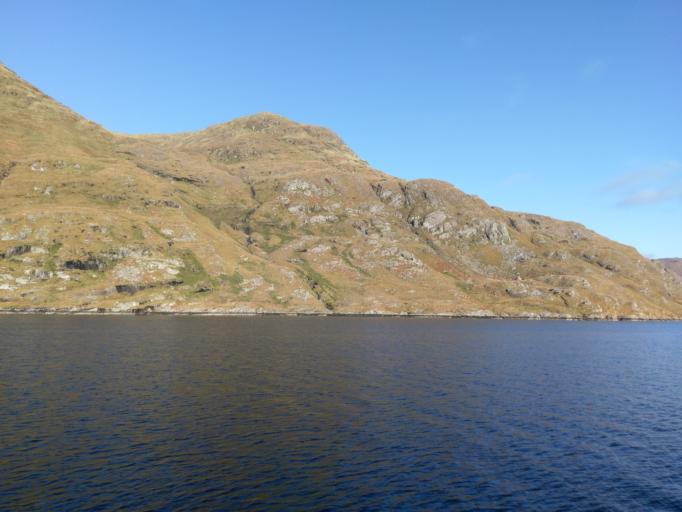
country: IE
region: Connaught
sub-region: County Galway
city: Clifden
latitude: 53.6191
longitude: -9.8365
